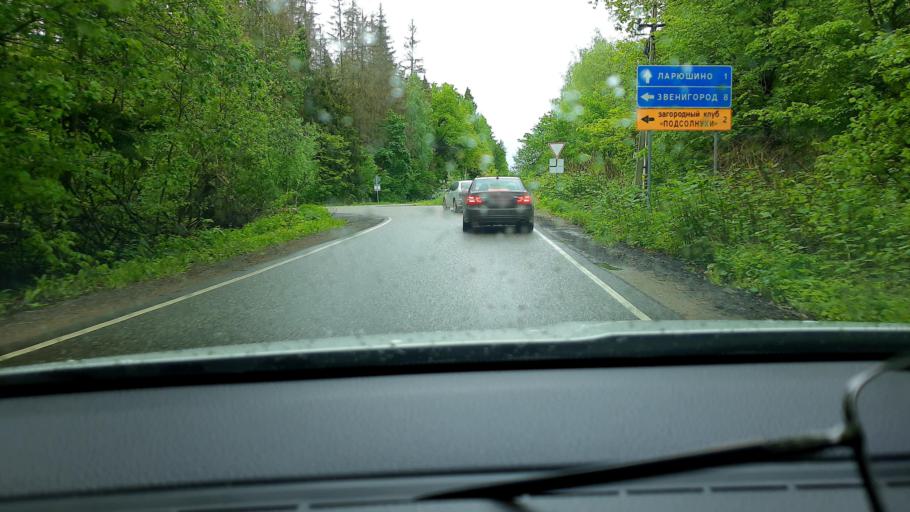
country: RU
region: Moskovskaya
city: Nikolina Gora
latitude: 55.7621
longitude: 36.9822
